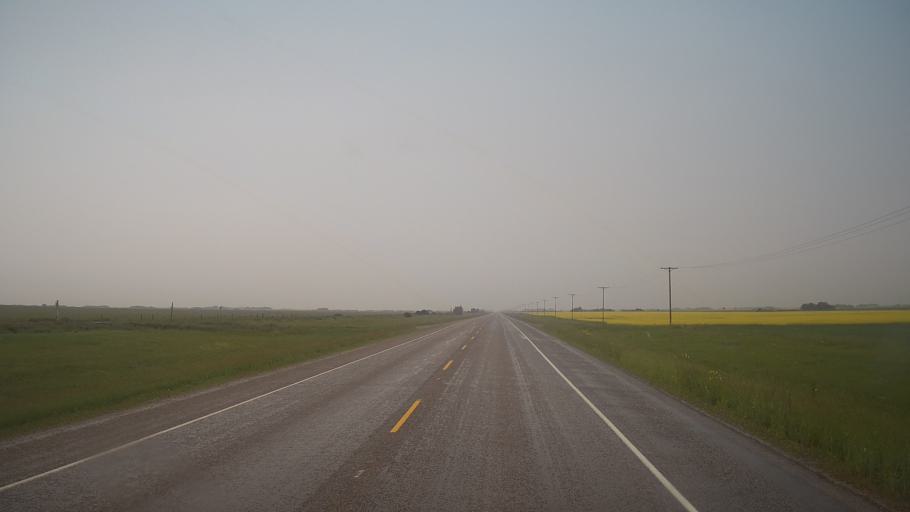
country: CA
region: Saskatchewan
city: Biggar
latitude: 52.1472
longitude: -108.2154
